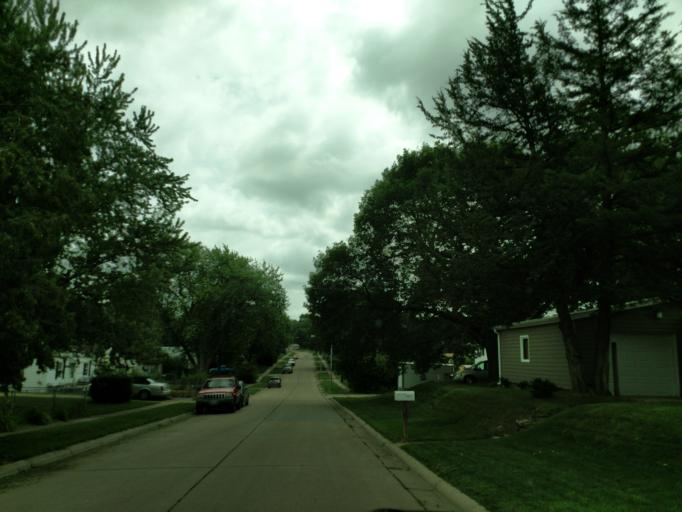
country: US
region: Nebraska
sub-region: Sarpy County
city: La Vista
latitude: 41.2093
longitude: -96.0006
